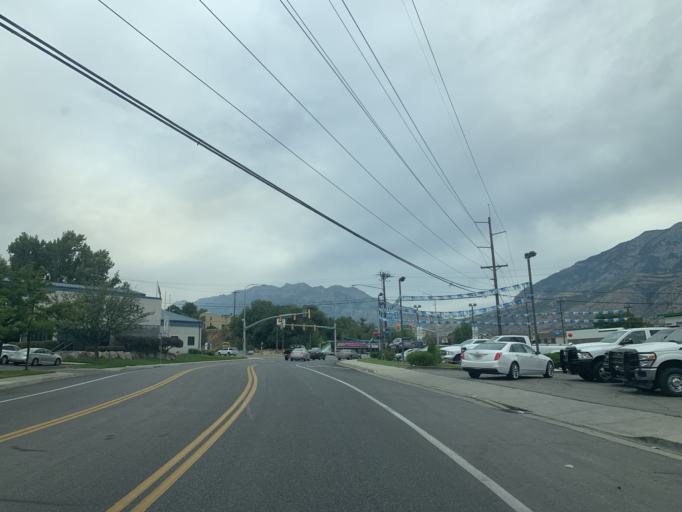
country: US
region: Utah
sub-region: Utah County
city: Provo
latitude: 40.2557
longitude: -111.6729
